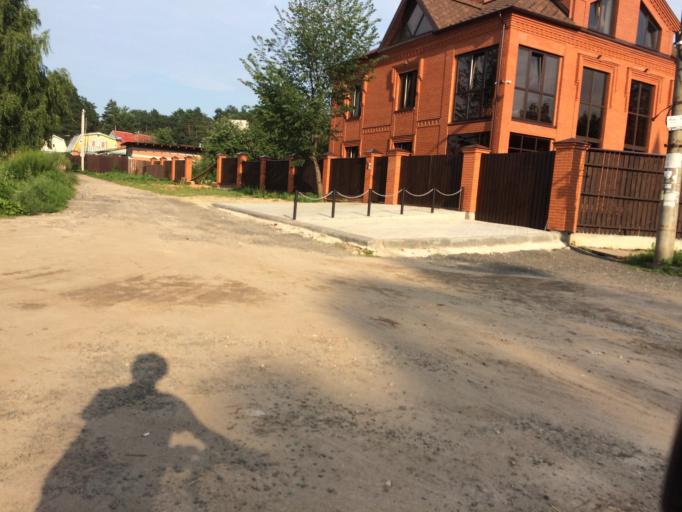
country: RU
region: Mariy-El
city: Yoshkar-Ola
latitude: 56.6171
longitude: 47.9443
